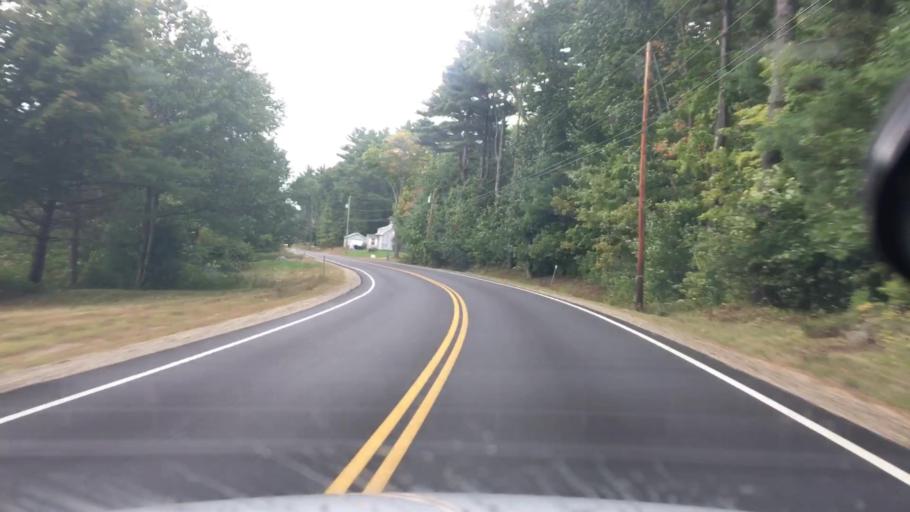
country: US
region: New Hampshire
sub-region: Carroll County
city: Sanbornville
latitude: 43.5320
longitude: -71.0228
